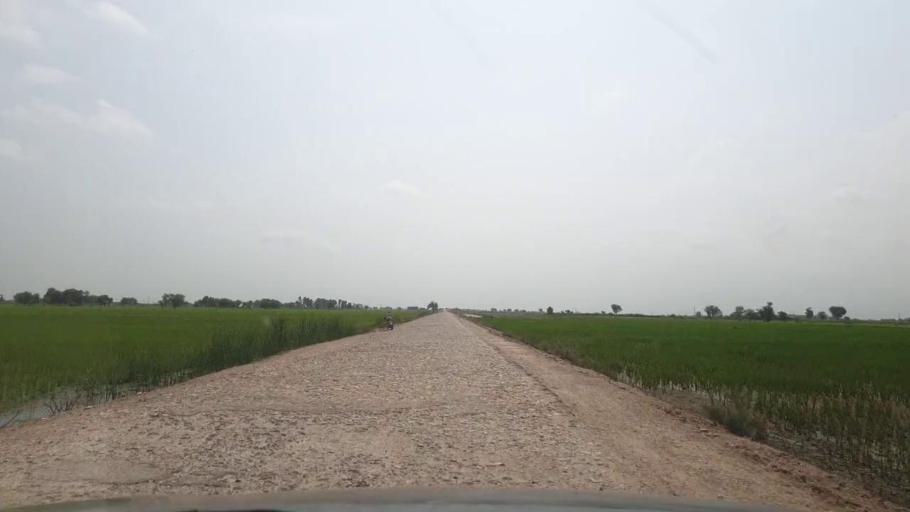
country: PK
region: Sindh
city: Ratodero
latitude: 27.8403
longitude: 68.3275
